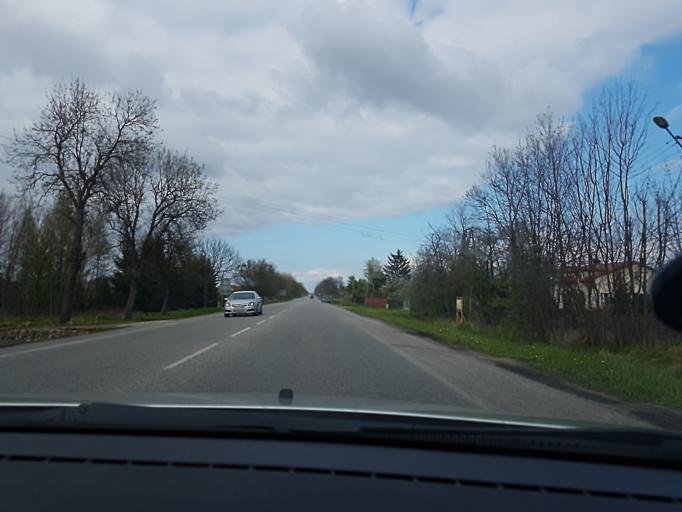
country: PL
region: Masovian Voivodeship
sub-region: Powiat sochaczewski
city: Sochaczew
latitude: 52.2197
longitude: 20.2051
